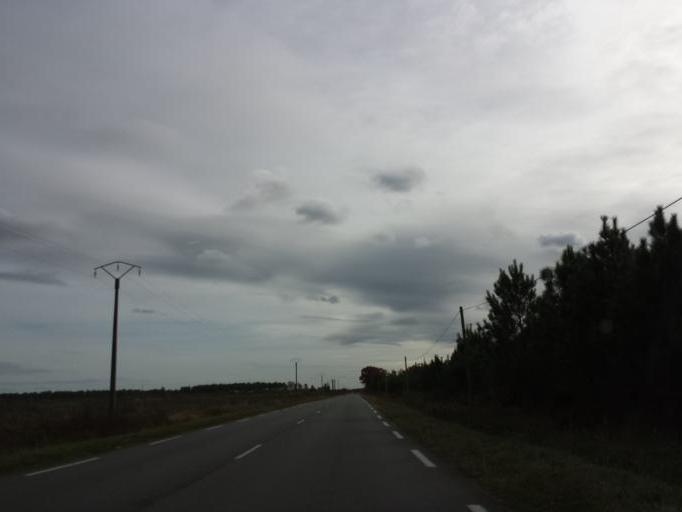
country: FR
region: Aquitaine
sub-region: Departement de la Gironde
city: Marcheprime
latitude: 44.7685
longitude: -0.9253
